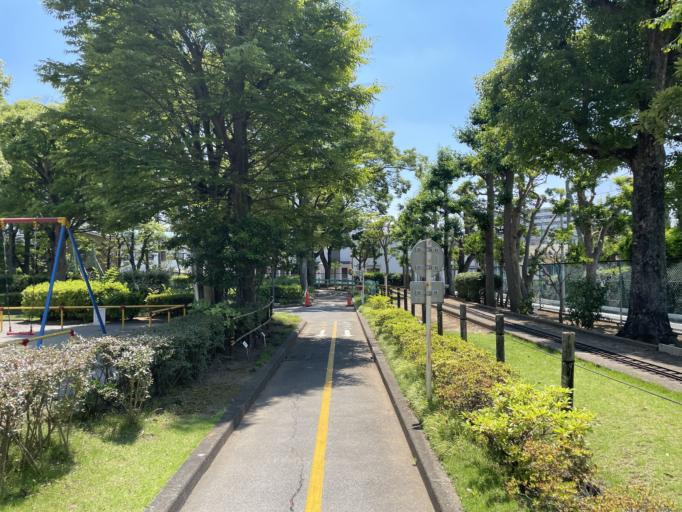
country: JP
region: Chiba
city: Matsudo
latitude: 35.7608
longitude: 139.8643
